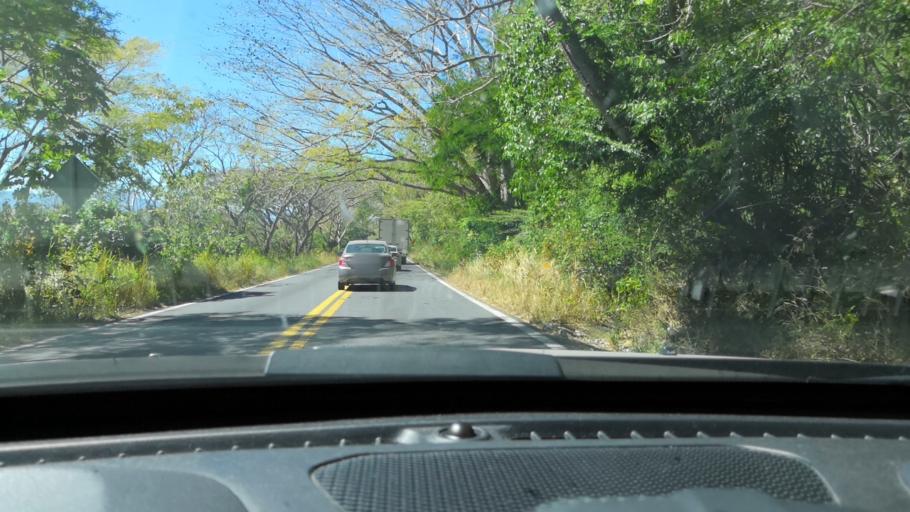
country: MX
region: Nayarit
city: Compostela
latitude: 21.2176
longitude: -104.9804
